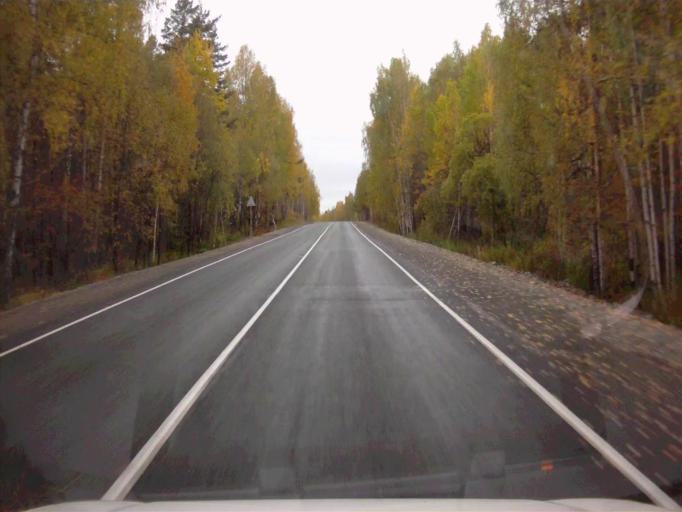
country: RU
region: Chelyabinsk
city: Nyazepetrovsk
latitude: 56.0564
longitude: 59.7358
